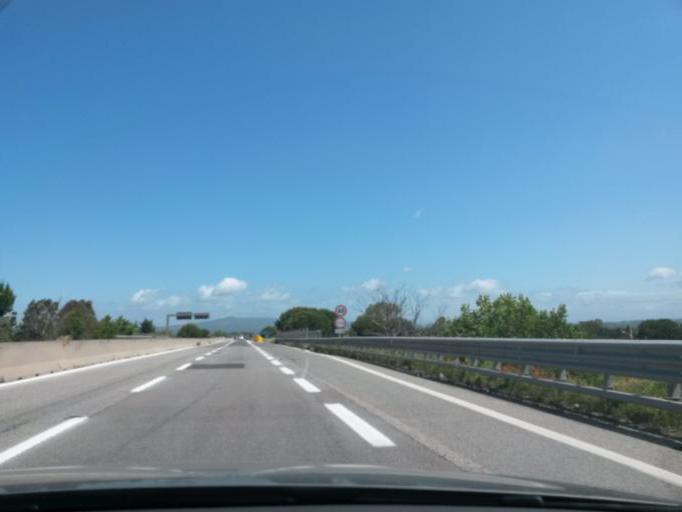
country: IT
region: Tuscany
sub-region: Provincia di Livorno
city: La California
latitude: 43.2779
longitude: 10.5398
